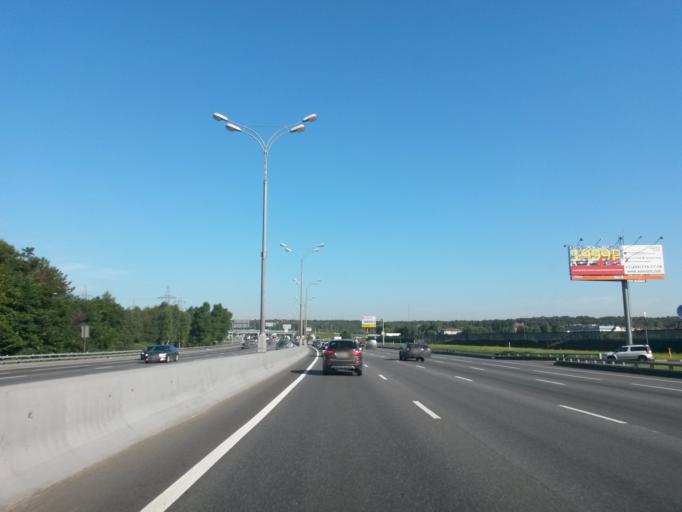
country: RU
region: Moscow
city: Gol'yanovo
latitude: 55.8259
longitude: 37.8341
